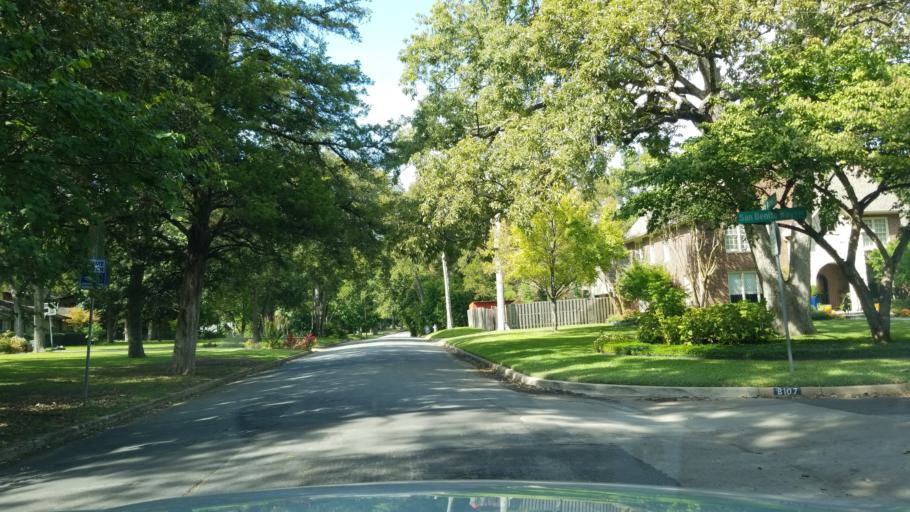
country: US
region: Texas
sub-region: Dallas County
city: Highland Park
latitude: 32.8086
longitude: -96.7196
